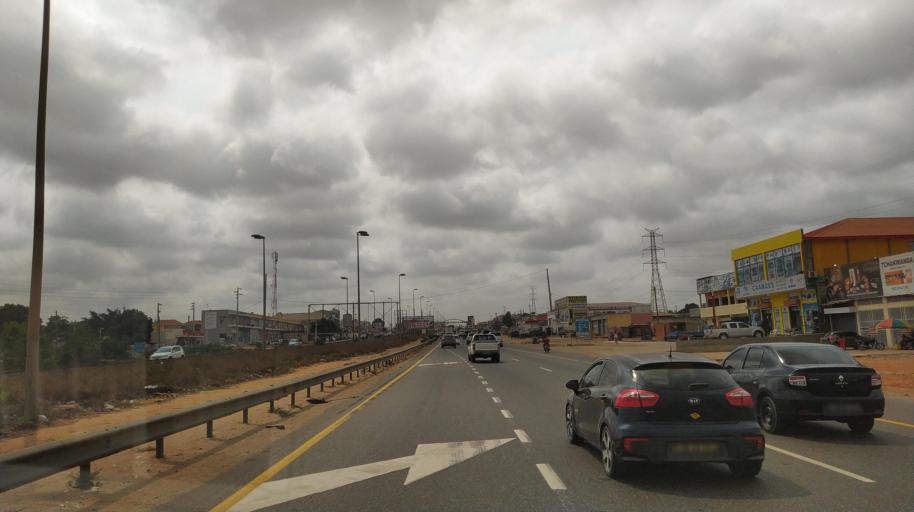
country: AO
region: Luanda
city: Luanda
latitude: -8.9731
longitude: 13.2999
